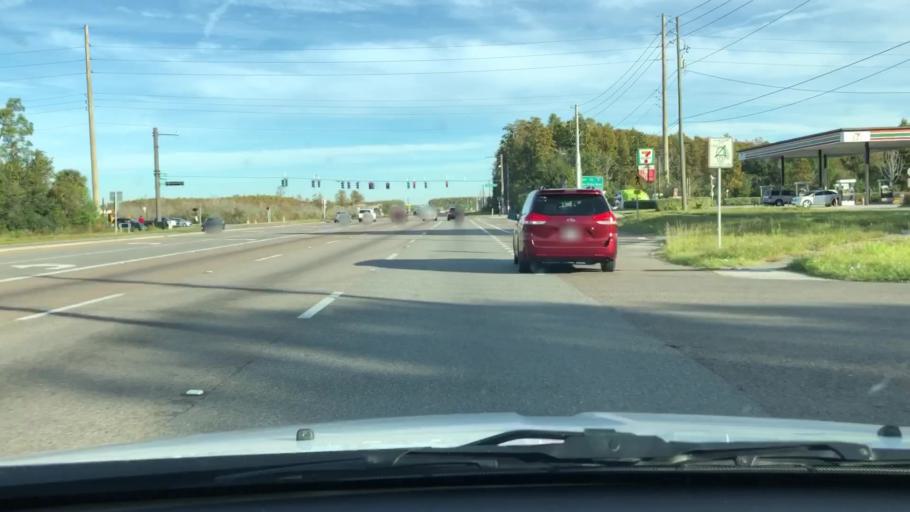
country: US
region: Florida
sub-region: Orange County
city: Hunters Creek
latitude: 28.3360
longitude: -81.4036
